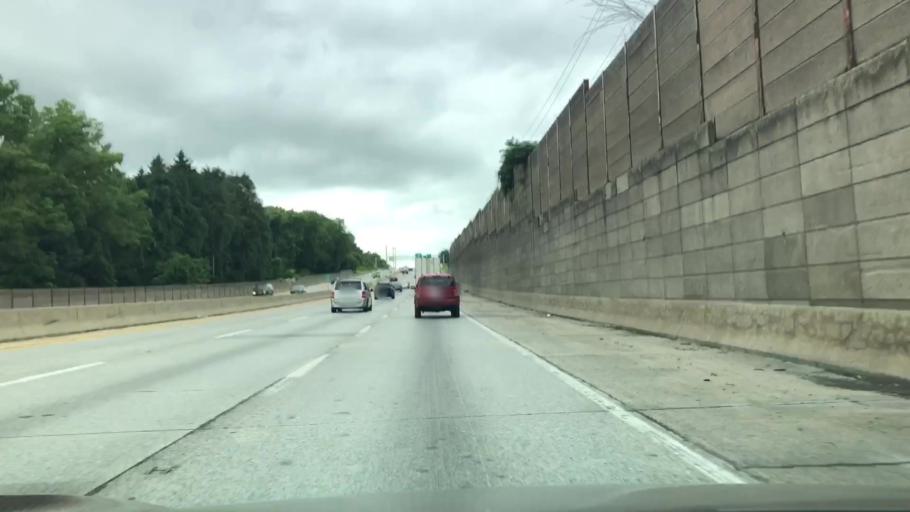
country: US
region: Pennsylvania
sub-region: Lehigh County
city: Dorneyville
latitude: 40.5666
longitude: -75.5054
